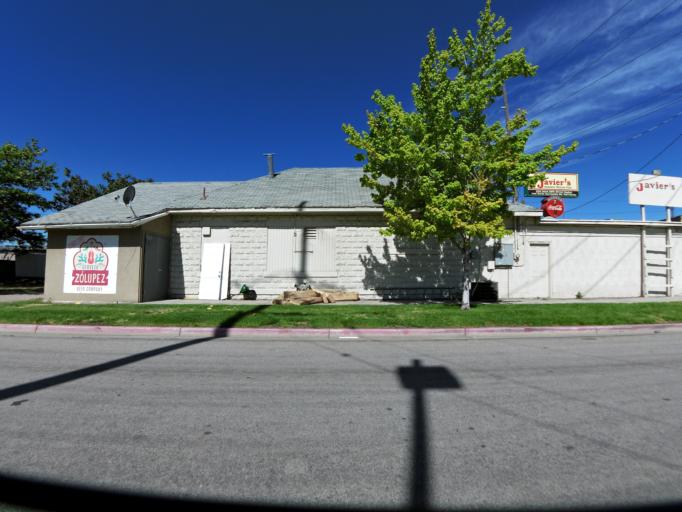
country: US
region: Utah
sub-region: Weber County
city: Ogden
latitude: 41.2122
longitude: -111.9822
